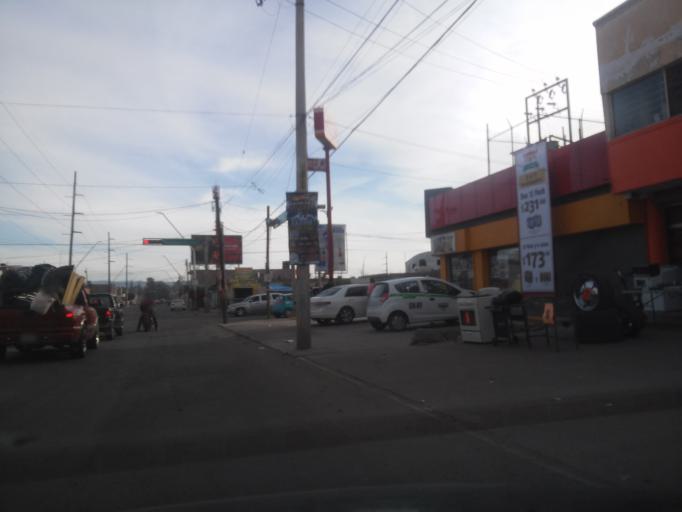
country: MX
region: Durango
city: Victoria de Durango
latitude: 24.0138
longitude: -104.6326
